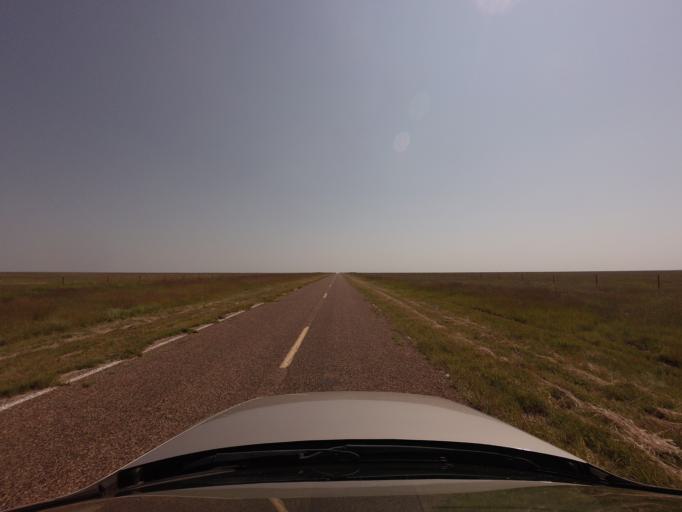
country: US
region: New Mexico
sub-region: Curry County
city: Cannon Air Force Base
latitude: 34.6333
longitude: -103.4467
